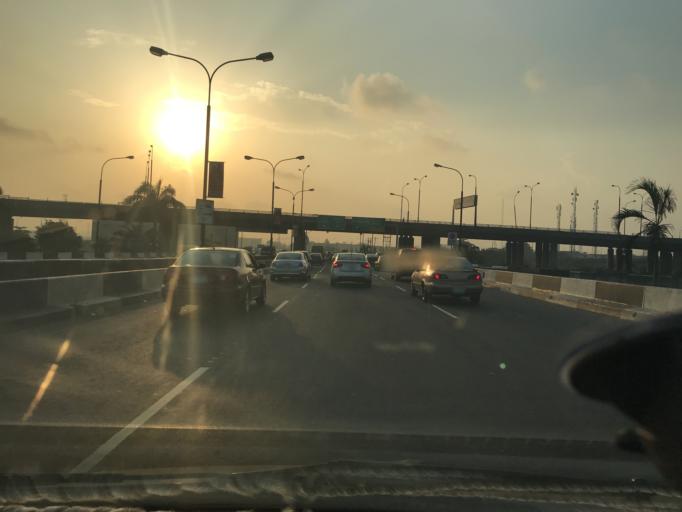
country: NG
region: Lagos
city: Lagos
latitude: 6.4621
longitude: 3.3950
